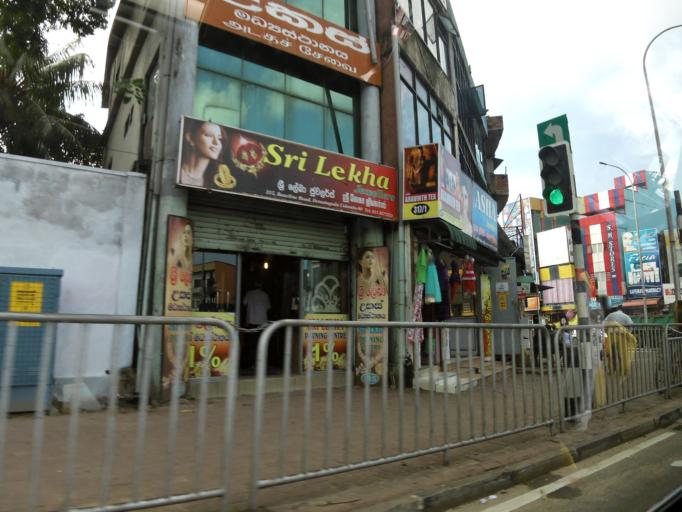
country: LK
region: Western
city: Kolonnawa
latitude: 6.9302
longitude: 79.8780
